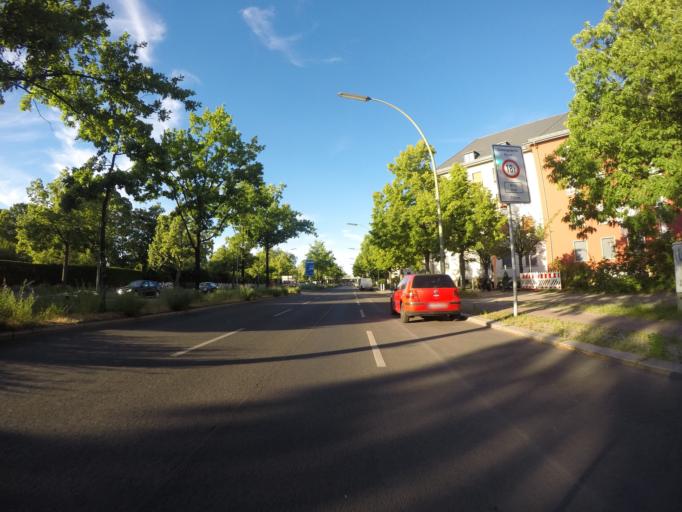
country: DE
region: Berlin
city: Schmargendorf
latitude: 52.4756
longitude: 13.3042
